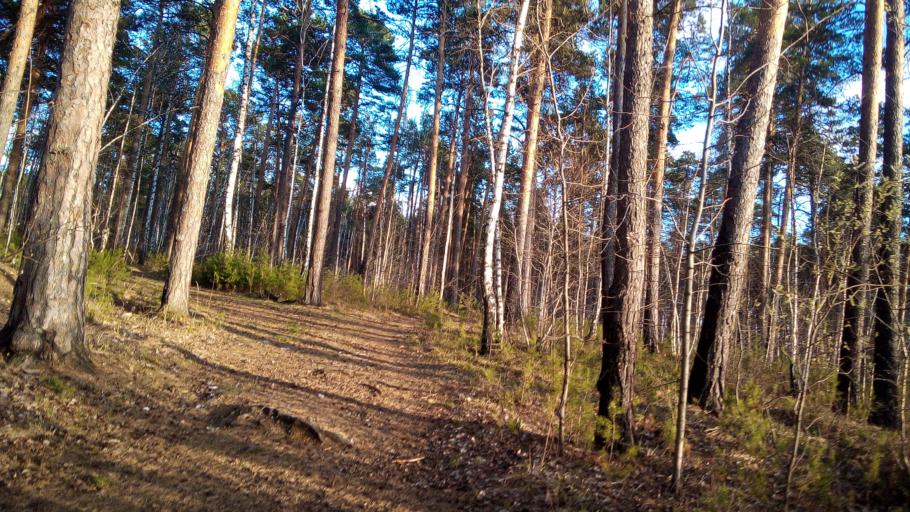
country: RU
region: Chelyabinsk
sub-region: Gorod Chelyabinsk
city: Chelyabinsk
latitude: 55.1619
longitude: 61.3228
